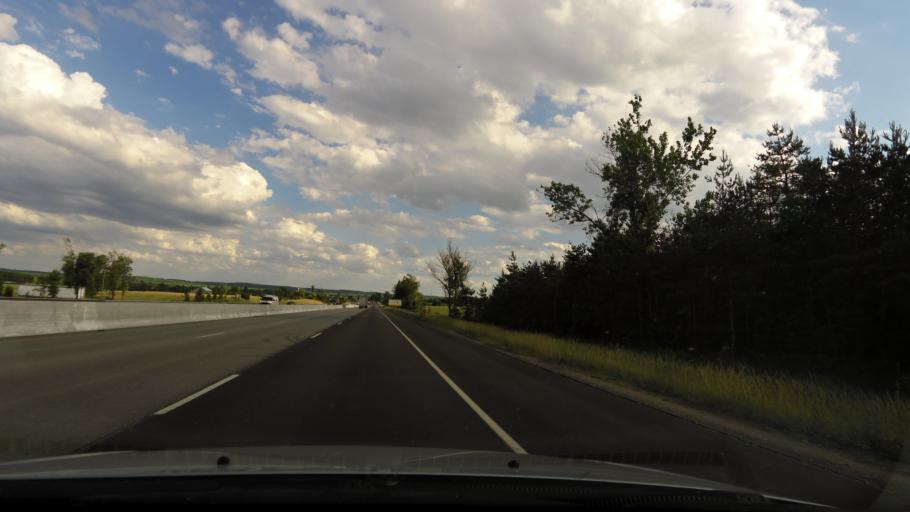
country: CA
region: Ontario
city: Innisfil
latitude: 44.2193
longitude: -79.6623
